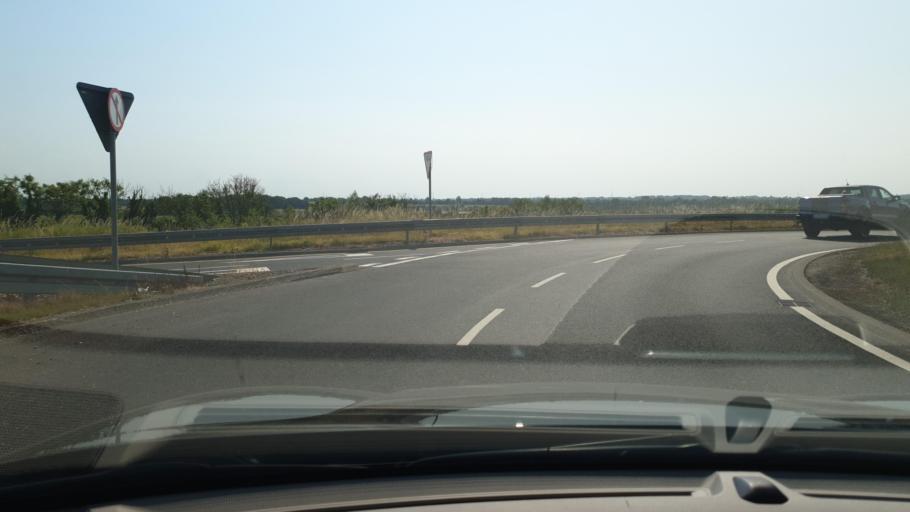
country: IE
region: Leinster
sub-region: An Mhi
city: Dunshaughlin
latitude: 53.5087
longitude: -6.5592
